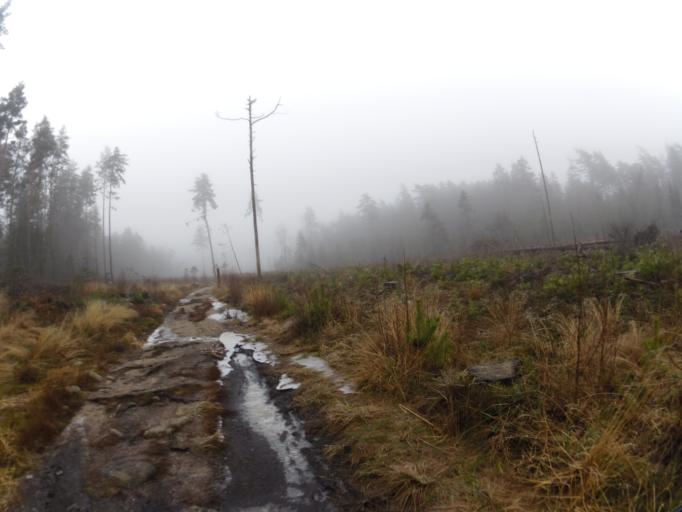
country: NO
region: Ostfold
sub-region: Fredrikstad
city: Fredrikstad
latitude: 59.2606
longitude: 10.9807
